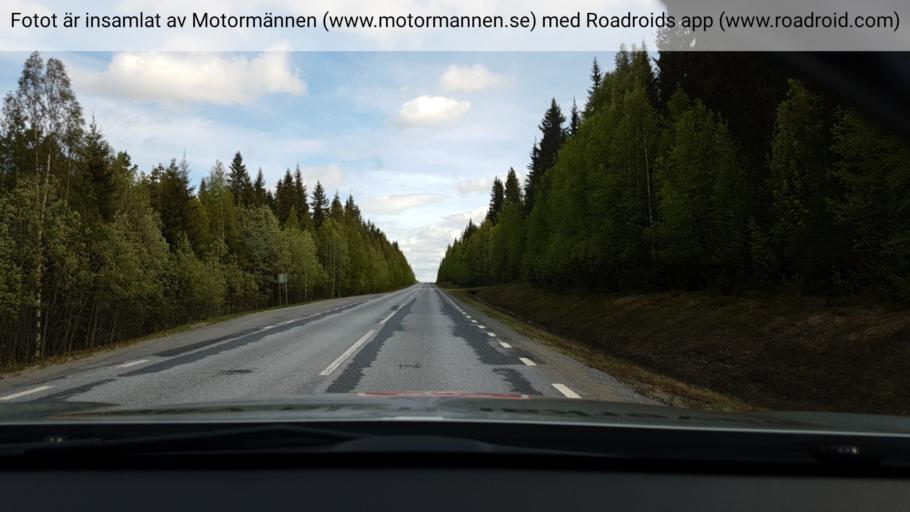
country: SE
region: Vaesterbotten
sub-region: Lycksele Kommun
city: Lycksele
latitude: 64.0523
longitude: 18.5562
